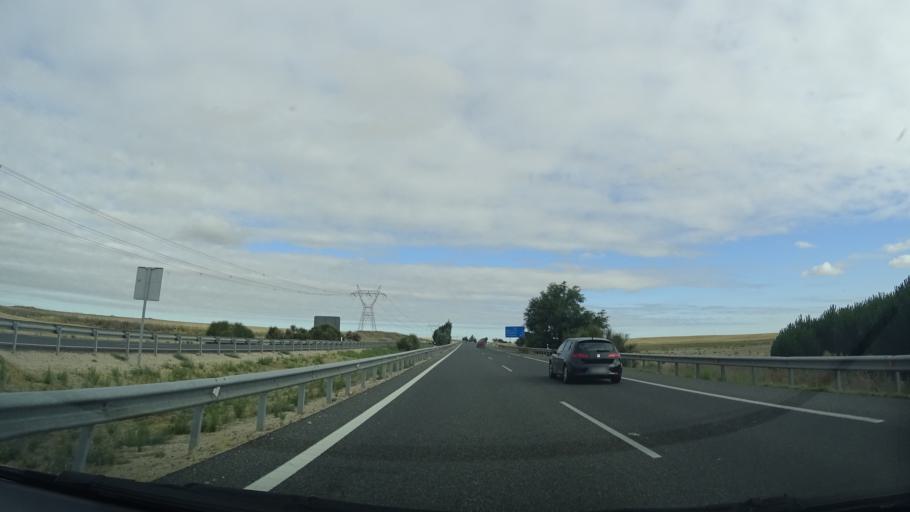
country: ES
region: Castille and Leon
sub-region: Provincia de Valladolid
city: San Pablo de la Moraleja
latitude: 41.1557
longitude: -4.7939
